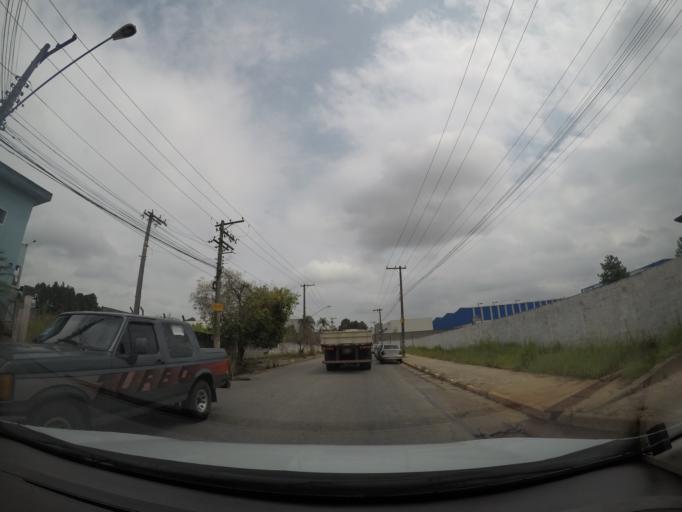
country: BR
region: Sao Paulo
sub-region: Itaquaquecetuba
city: Itaquaquecetuba
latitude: -23.4273
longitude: -46.3943
